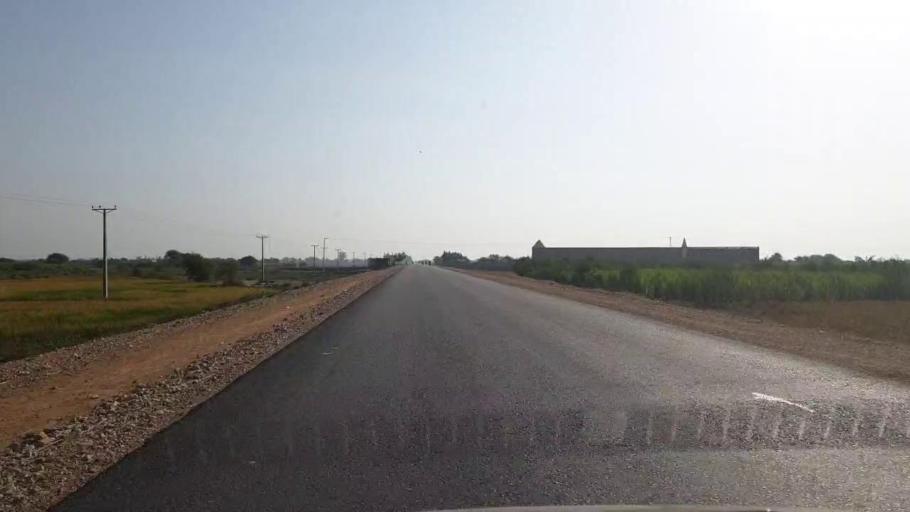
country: PK
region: Sindh
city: Badin
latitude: 24.6600
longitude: 68.8875
